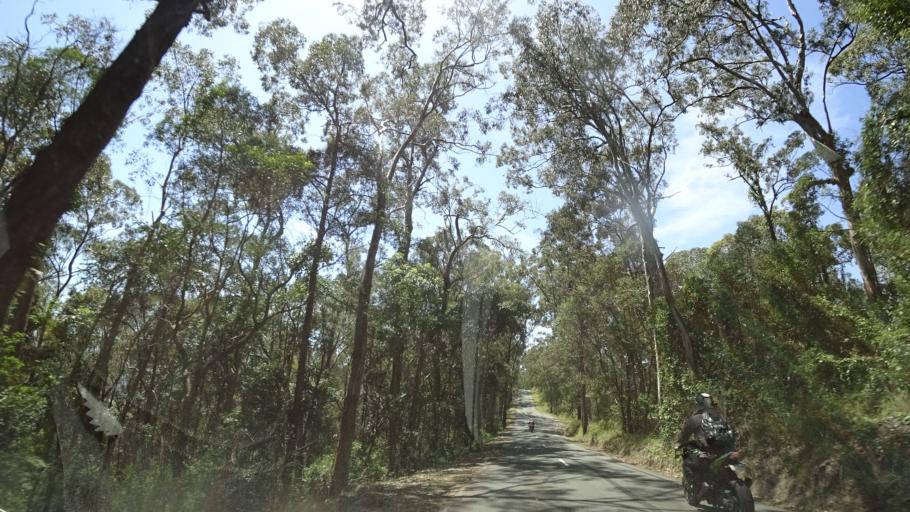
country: AU
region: Queensland
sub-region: Moreton Bay
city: Highvale
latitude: -27.4164
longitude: 152.8318
